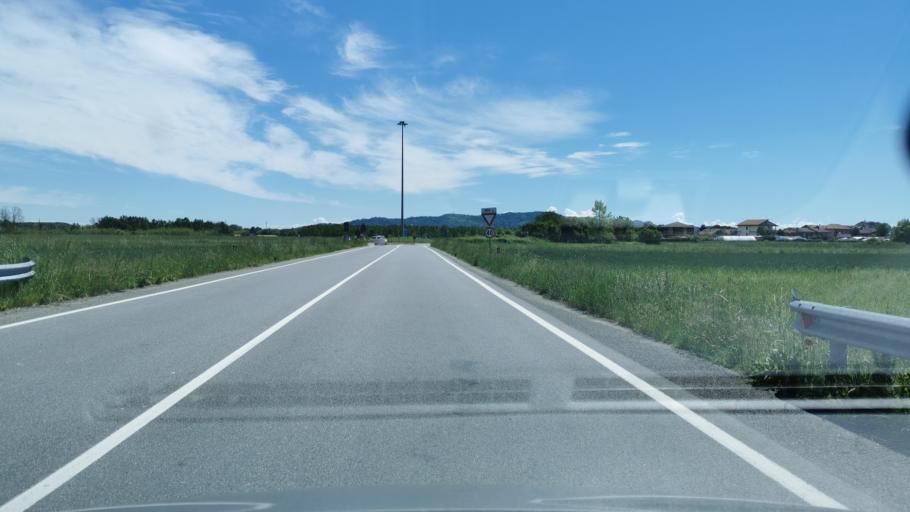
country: IT
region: Piedmont
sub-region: Provincia di Torino
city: Volpiano
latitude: 45.2079
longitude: 7.7873
